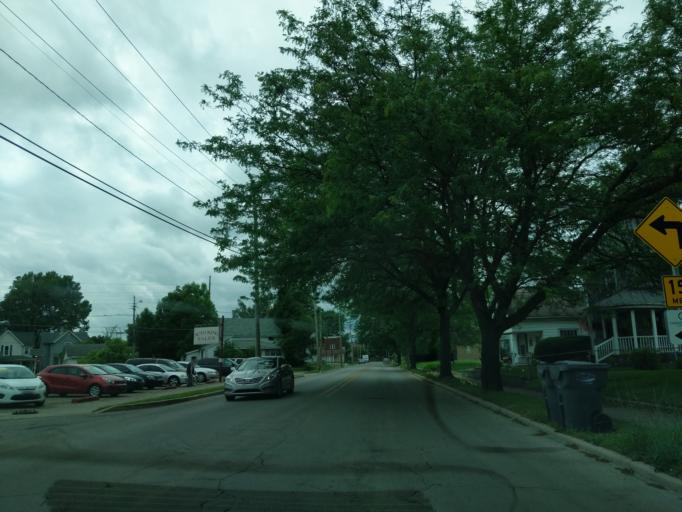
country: US
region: Indiana
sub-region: Madison County
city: Anderson
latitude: 40.1014
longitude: -85.6714
